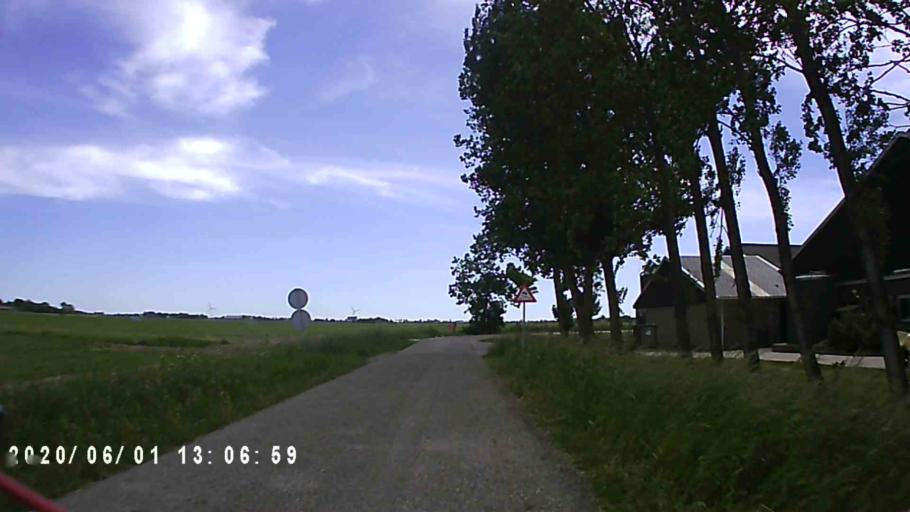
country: NL
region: Friesland
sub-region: Gemeente Franekeradeel
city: Tzum
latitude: 53.1332
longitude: 5.5534
